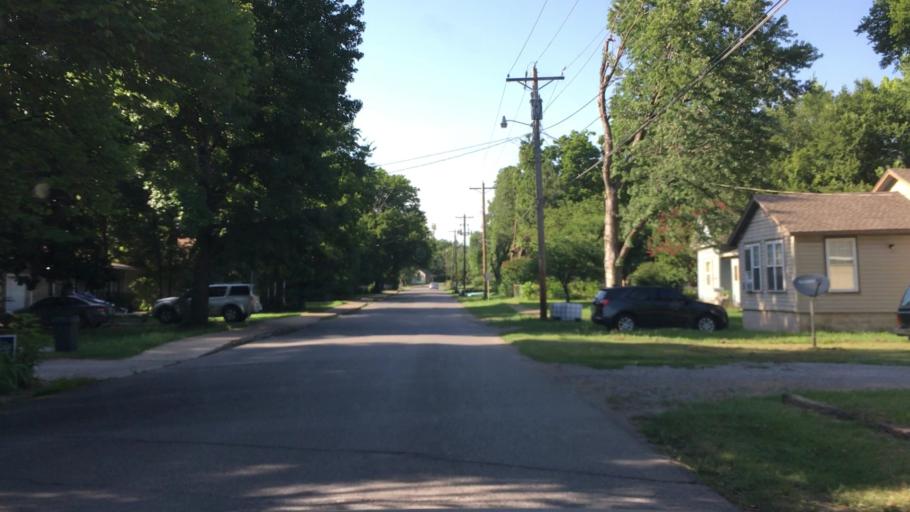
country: US
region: Oklahoma
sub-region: Cherokee County
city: Tahlequah
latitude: 35.9045
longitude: -94.9757
